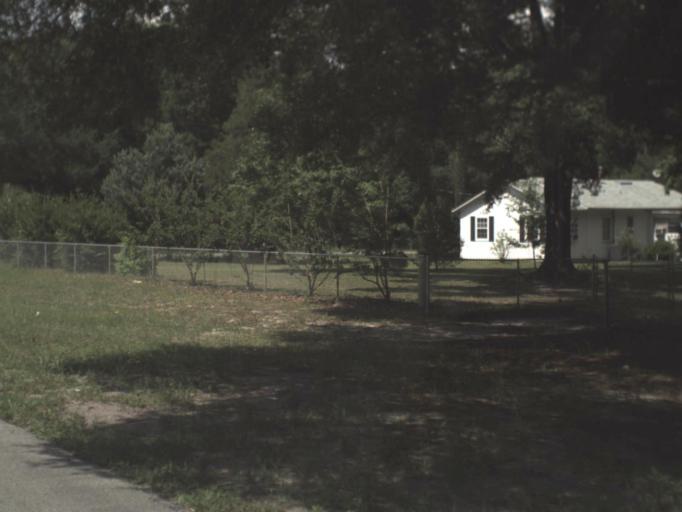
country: US
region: Florida
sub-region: Bradford County
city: Starke
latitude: 29.9534
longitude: -82.0163
